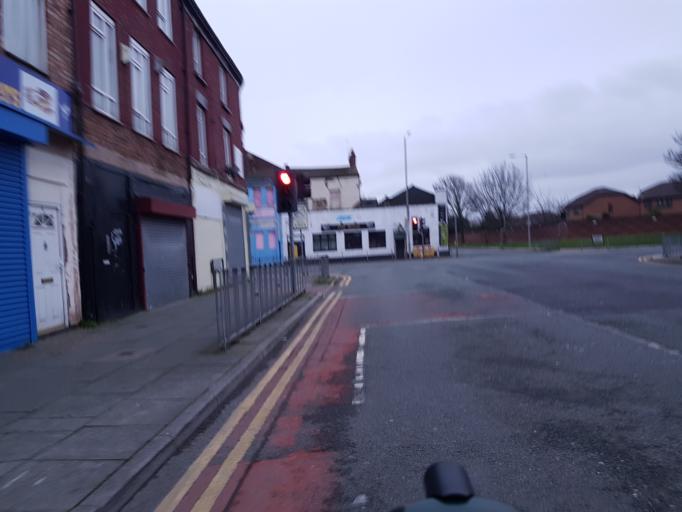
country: GB
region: England
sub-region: Liverpool
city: Liverpool
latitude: 53.4226
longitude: -2.9606
